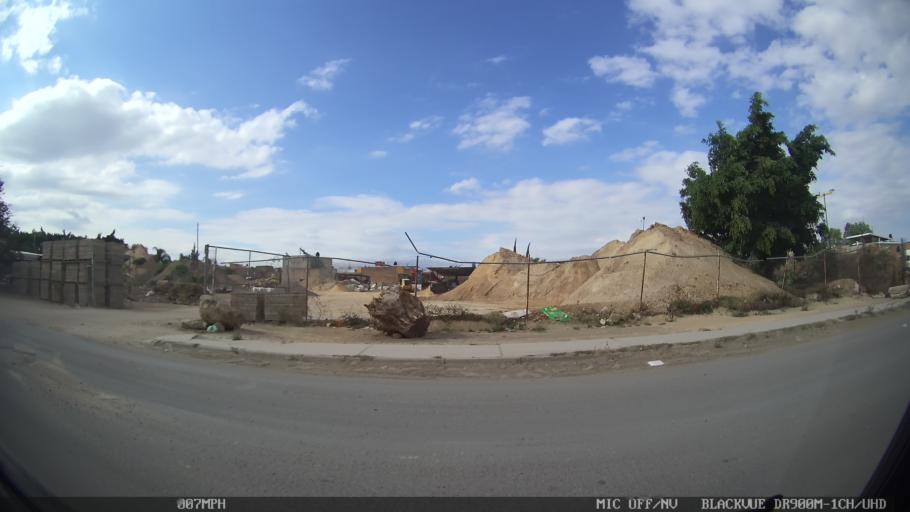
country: MX
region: Jalisco
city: Tonala
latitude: 20.6592
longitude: -103.2490
